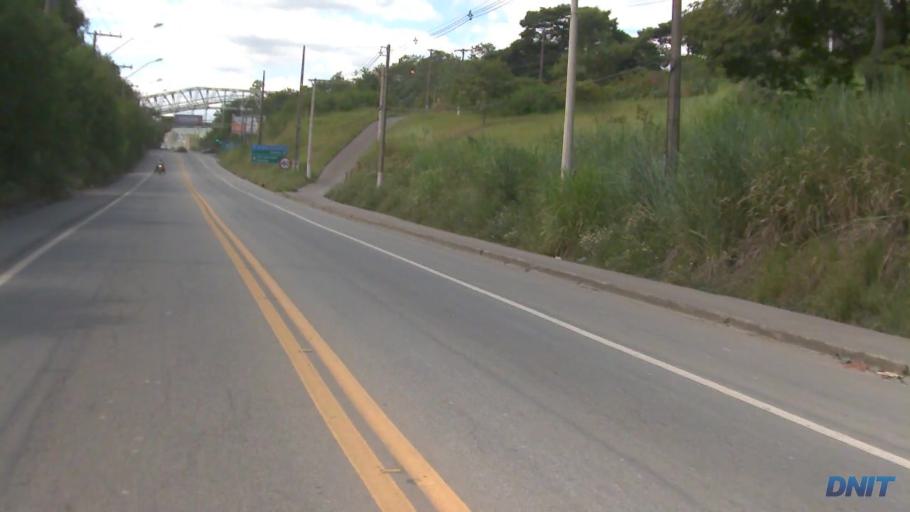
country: BR
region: Minas Gerais
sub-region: Coronel Fabriciano
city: Coronel Fabriciano
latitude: -19.5289
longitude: -42.6538
